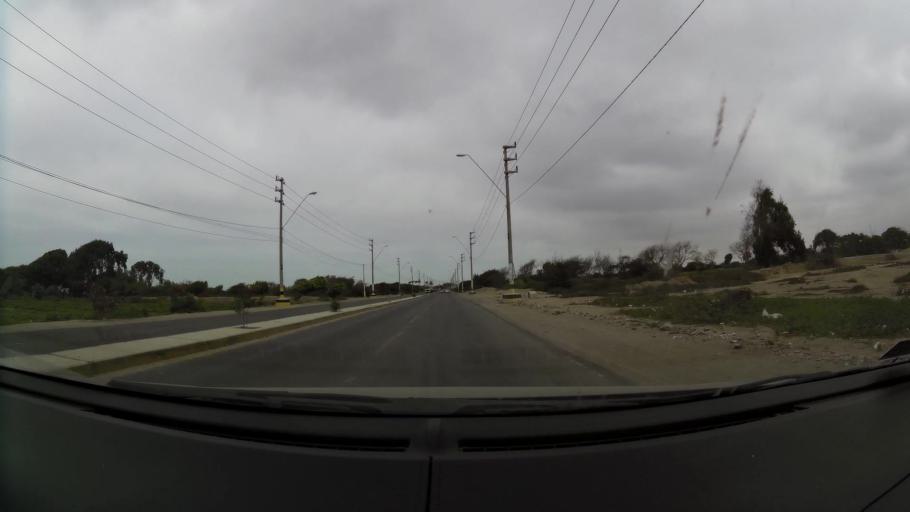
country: PE
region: La Libertad
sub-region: Provincia de Trujillo
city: La Esperanza
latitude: -8.0930
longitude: -79.0769
